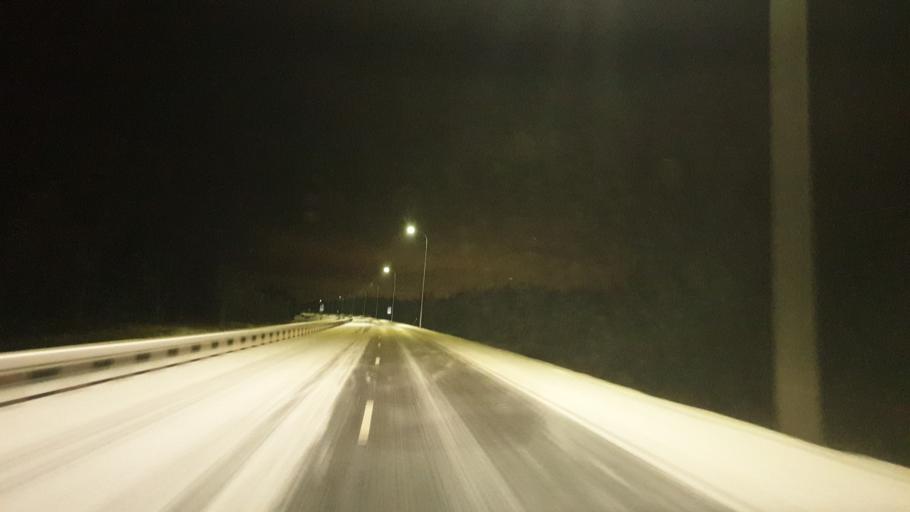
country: FI
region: Northern Ostrobothnia
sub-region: Oulu
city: Haukipudas
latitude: 65.2221
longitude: 25.3967
